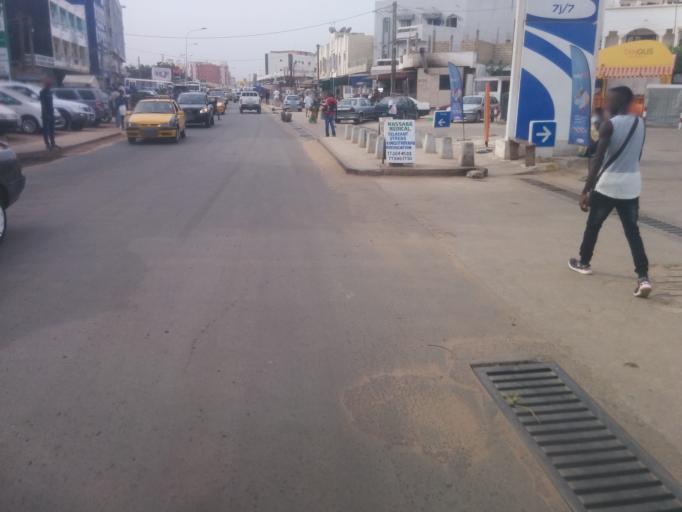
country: SN
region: Dakar
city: Grand Dakar
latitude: 14.7346
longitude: -17.4560
